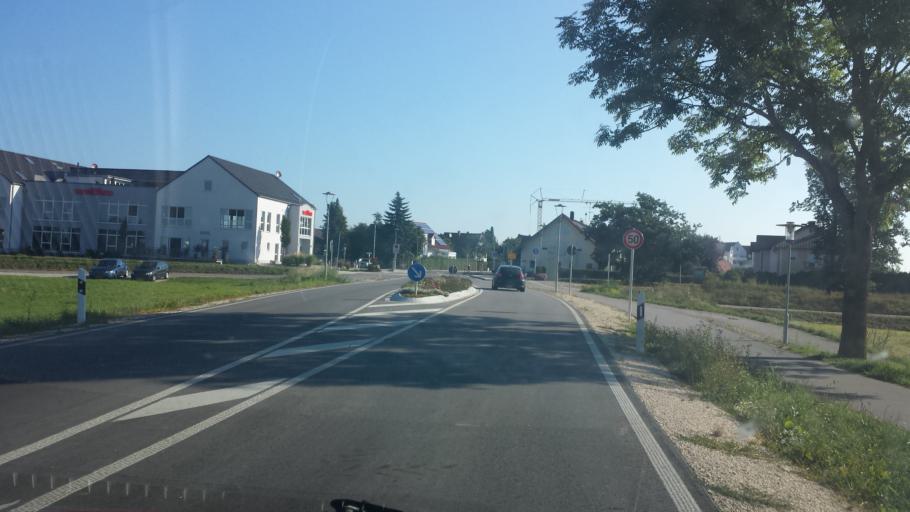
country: DE
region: Bavaria
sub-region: Lower Bavaria
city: Neustadt an der Donau
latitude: 48.8192
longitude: 11.7767
